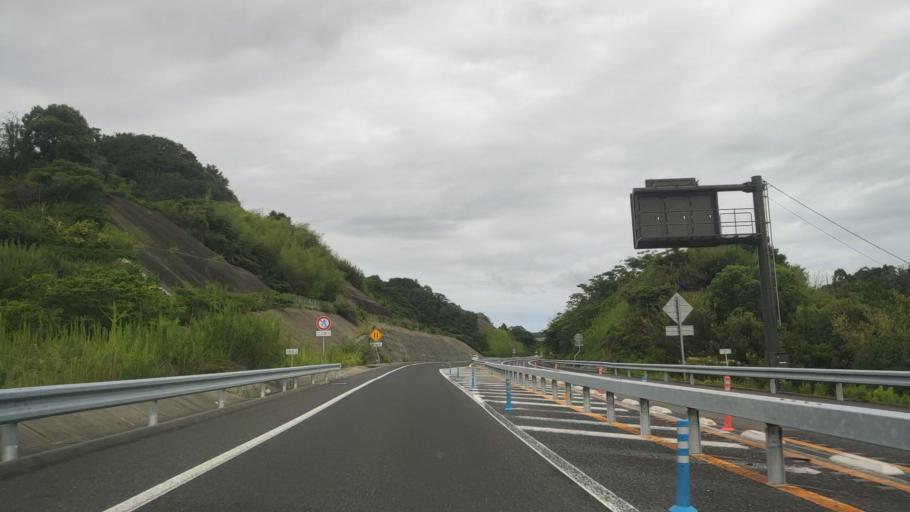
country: JP
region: Wakayama
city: Tanabe
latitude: 33.7579
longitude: 135.3542
